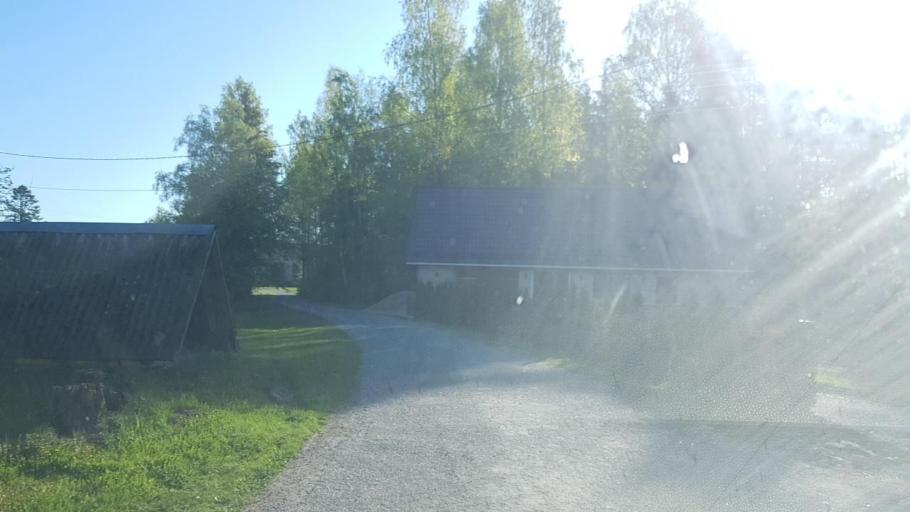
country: EE
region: Laeaene-Virumaa
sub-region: Viru-Nigula vald
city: Kunda
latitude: 59.3235
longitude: 26.6327
